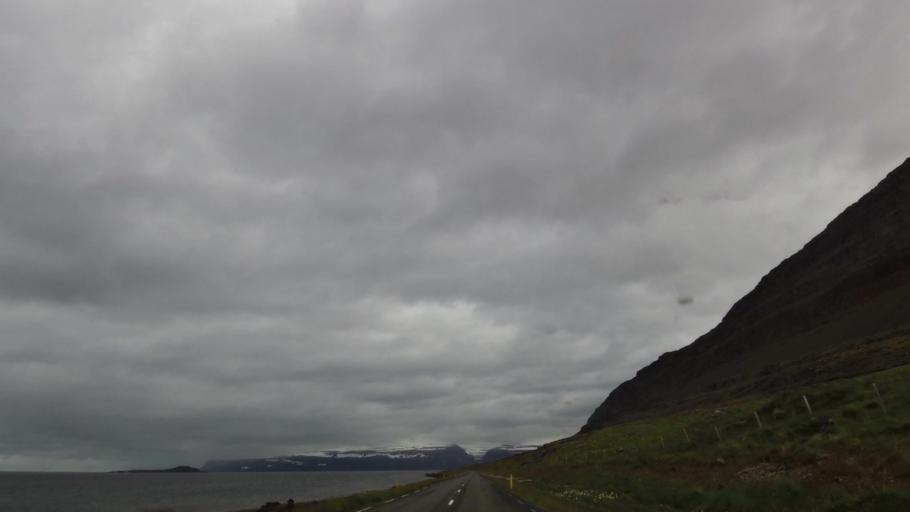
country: IS
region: Westfjords
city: Isafjoerdur
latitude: 66.0105
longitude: -22.7824
